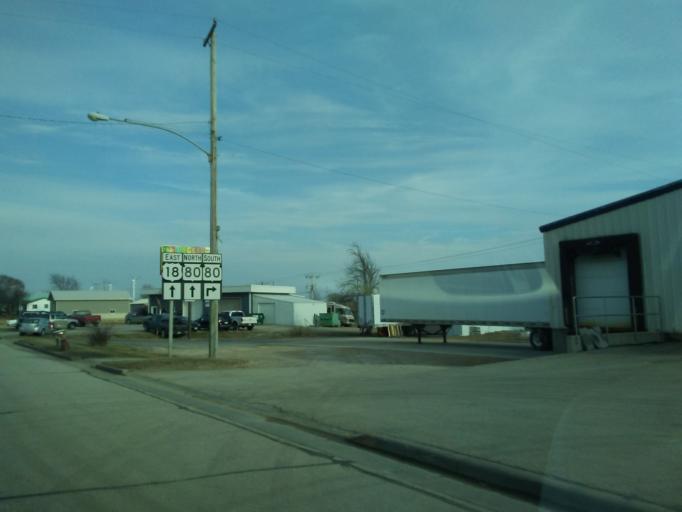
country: US
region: Wisconsin
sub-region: Grant County
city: Muscoda
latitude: 42.9660
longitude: -90.4319
